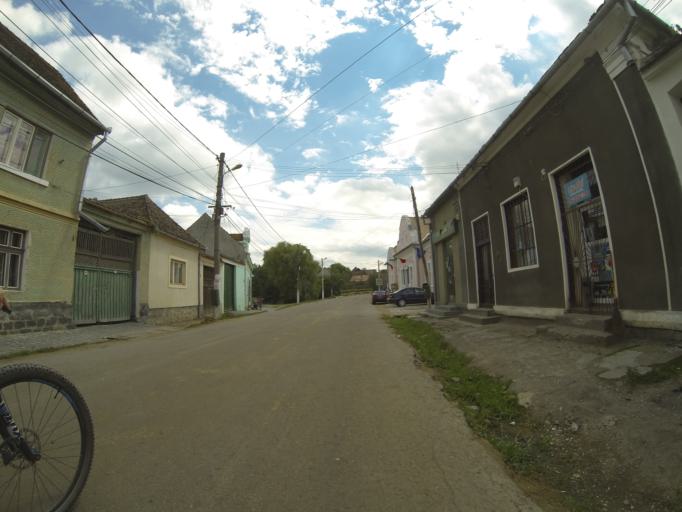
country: RO
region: Brasov
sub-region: Comuna Hoghiz
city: Hoghiz
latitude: 46.0249
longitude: 25.4050
